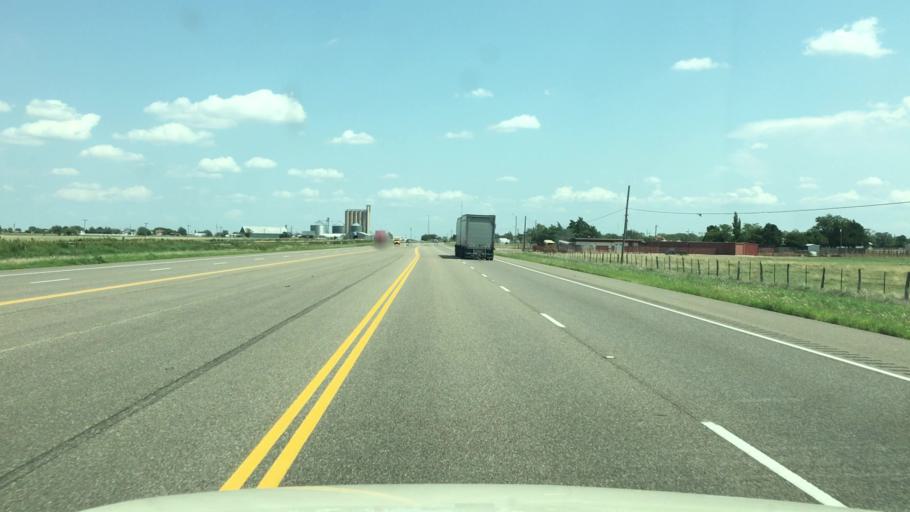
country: US
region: Texas
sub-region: Armstrong County
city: Claude
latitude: 35.1162
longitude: -101.3728
